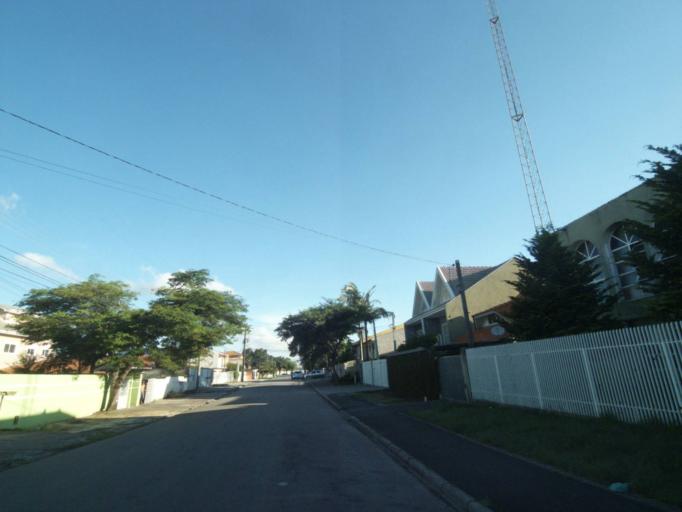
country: BR
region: Parana
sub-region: Pinhais
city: Pinhais
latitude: -25.4666
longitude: -49.2016
